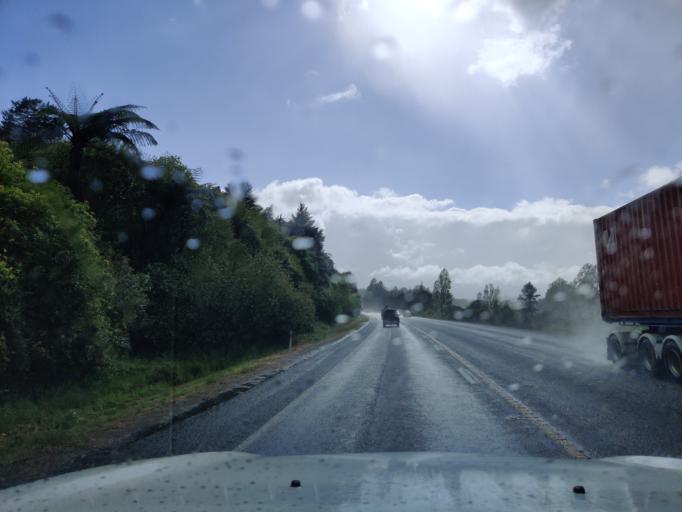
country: NZ
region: Waikato
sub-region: Matamata-Piako District
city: Matamata
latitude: -37.9512
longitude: 175.6328
